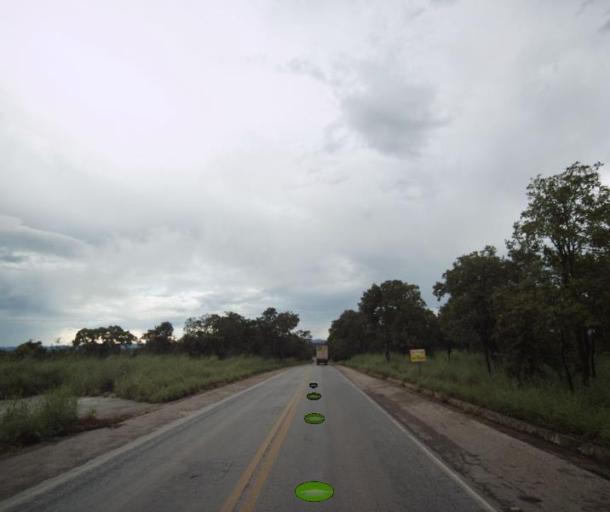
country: BR
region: Goias
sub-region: Porangatu
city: Porangatu
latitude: -13.6459
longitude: -49.0396
